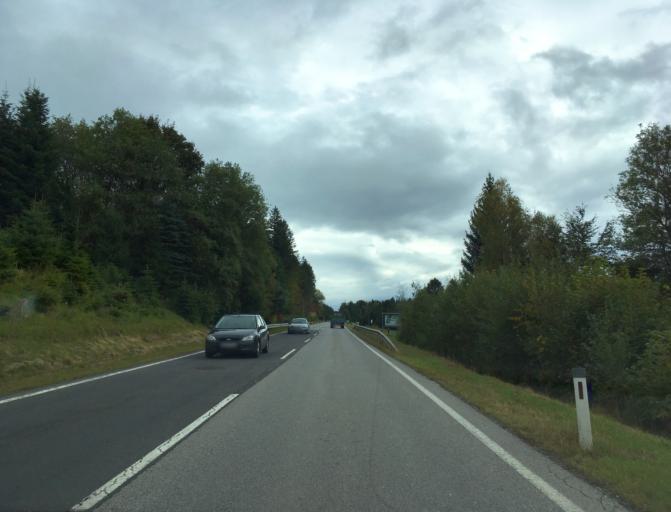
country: AT
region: Lower Austria
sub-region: Politischer Bezirk Neunkirchen
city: Thomasberg
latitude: 47.5449
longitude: 16.1492
